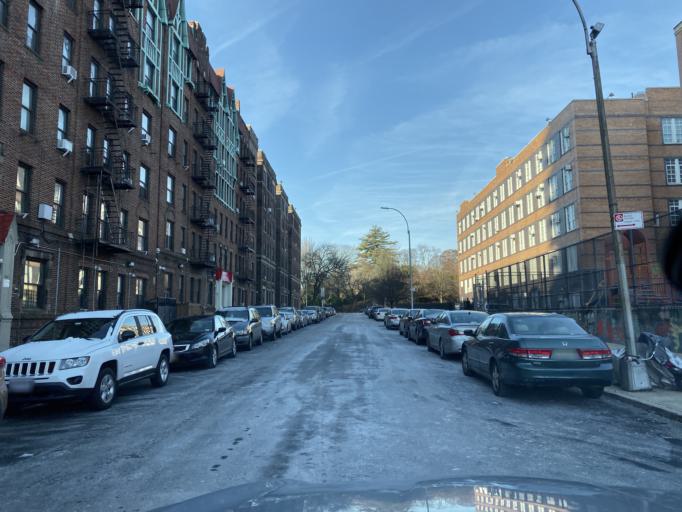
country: US
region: New York
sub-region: Kings County
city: Brooklyn
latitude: 40.6683
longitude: -73.9605
